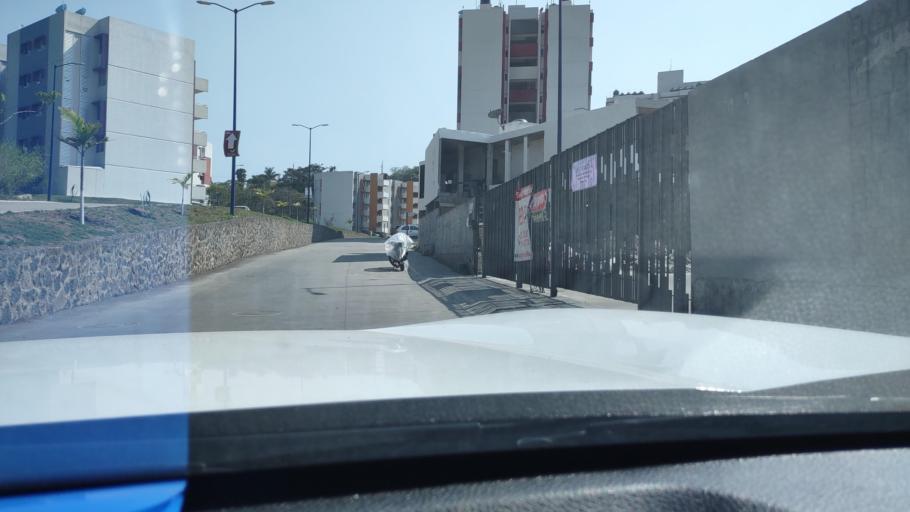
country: MX
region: Veracruz
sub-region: Emiliano Zapata
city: Jacarandas
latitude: 19.5137
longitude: -96.8480
